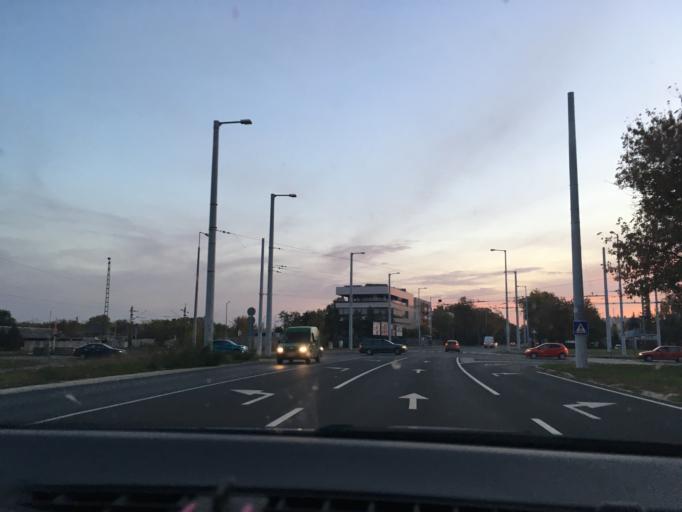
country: HU
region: Hajdu-Bihar
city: Debrecen
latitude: 47.5537
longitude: 21.6499
